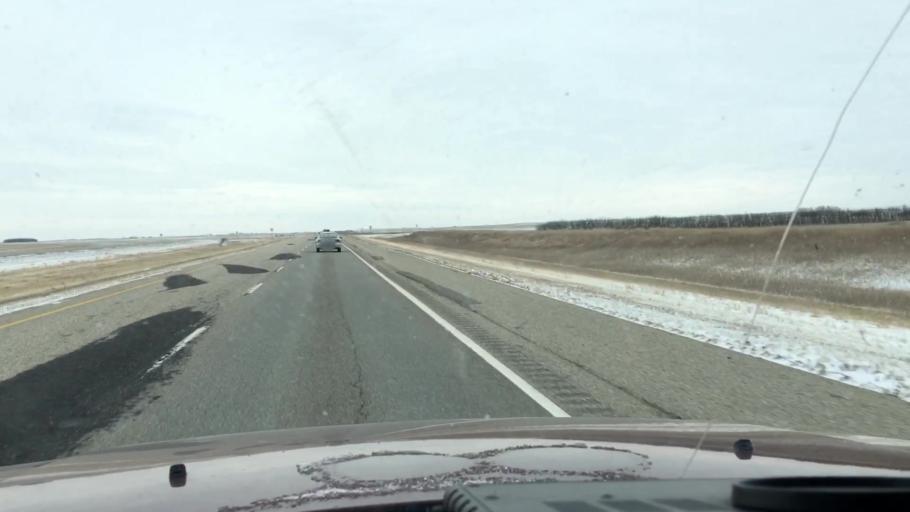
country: CA
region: Saskatchewan
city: Saskatoon
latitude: 51.4658
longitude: -106.2410
